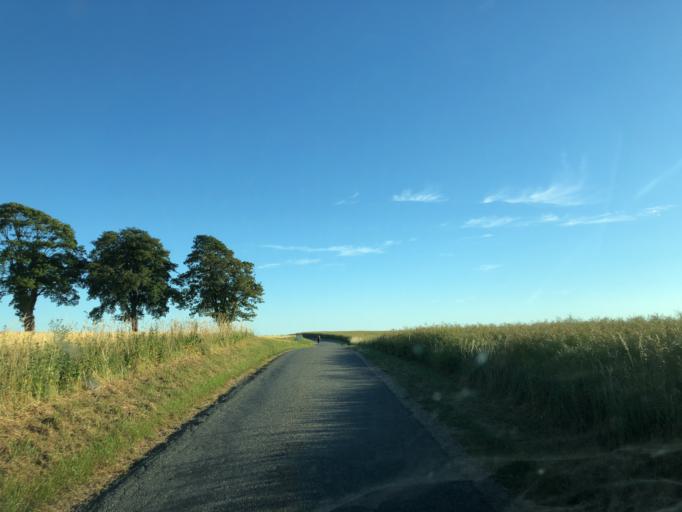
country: DK
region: Central Jutland
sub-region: Horsens Kommune
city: Horsens
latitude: 55.9016
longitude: 9.8620
